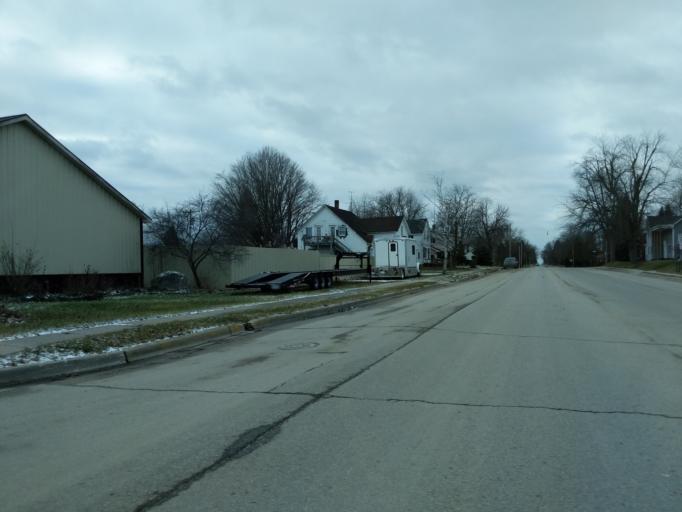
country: US
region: Michigan
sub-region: Sanilac County
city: Marlette
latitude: 43.3278
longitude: -83.0812
